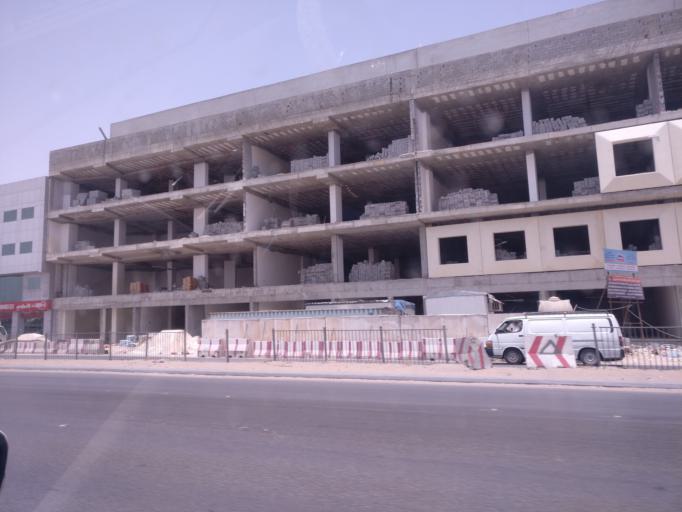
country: SA
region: Ar Riyad
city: Riyadh
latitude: 24.6084
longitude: 46.7071
